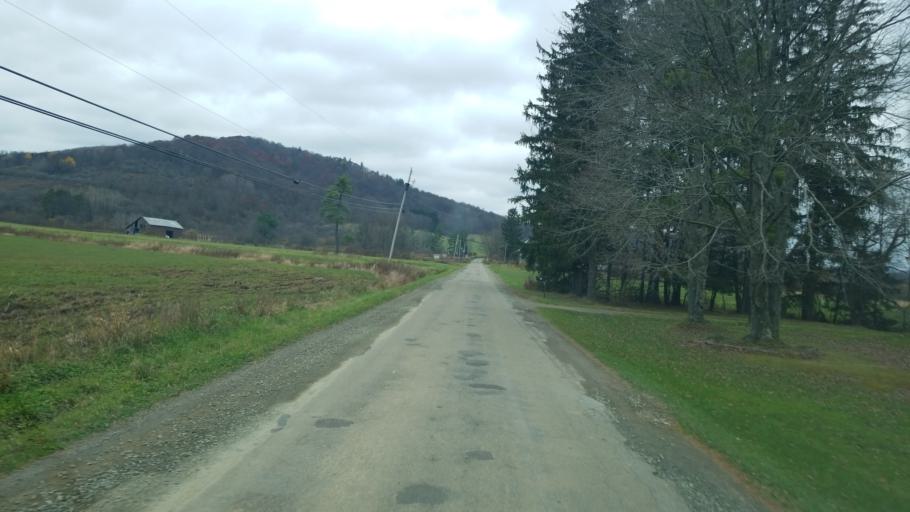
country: US
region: Pennsylvania
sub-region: McKean County
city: Smethport
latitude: 41.7826
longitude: -78.4220
